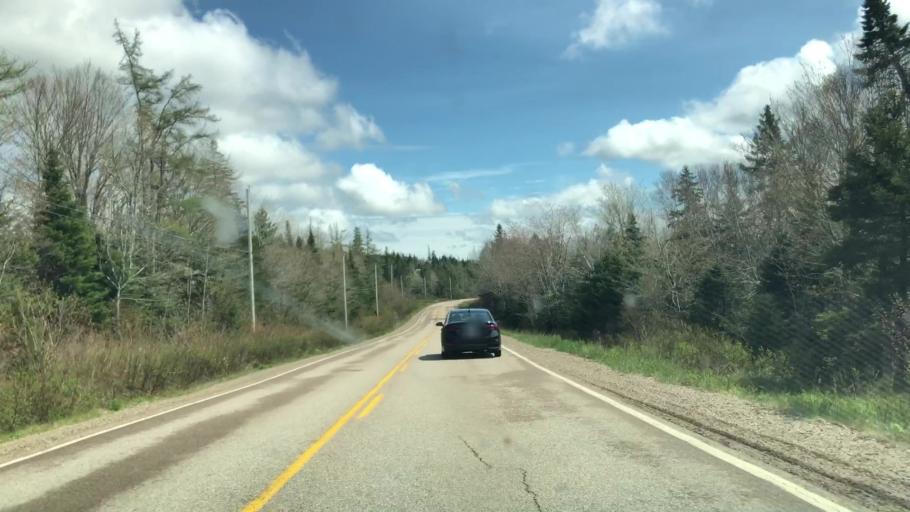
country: CA
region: Nova Scotia
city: Antigonish
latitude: 45.2123
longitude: -62.0050
